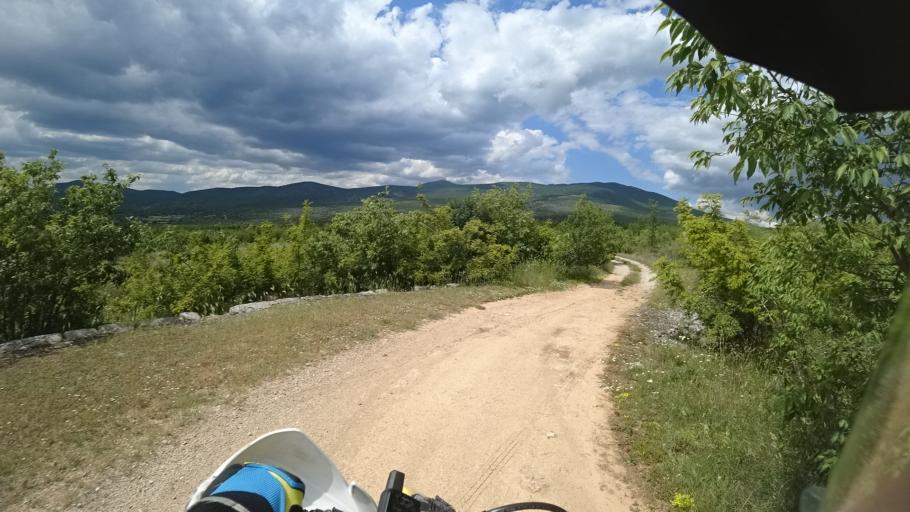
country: HR
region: Sibensko-Kniniska
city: Kistanje
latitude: 44.0887
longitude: 16.0484
